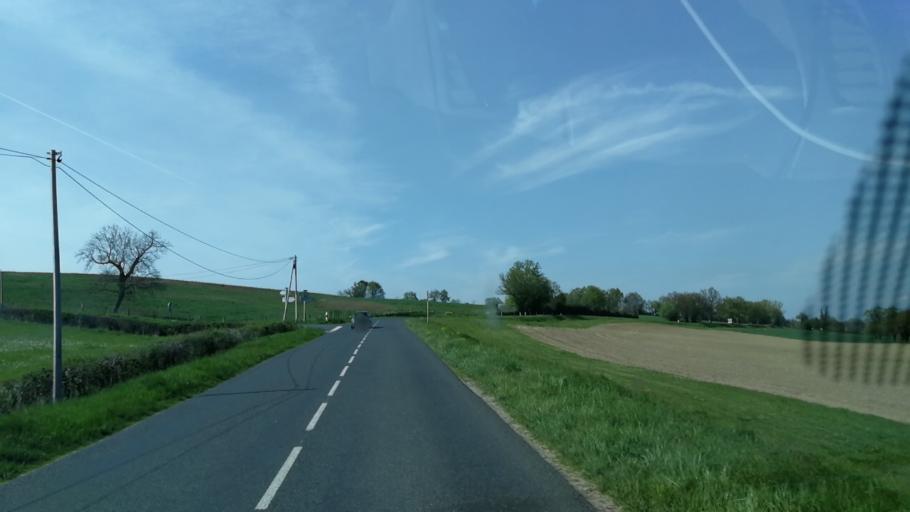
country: FR
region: Auvergne
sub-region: Departement de l'Allier
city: Saint-Gerand-le-Puy
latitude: 46.3568
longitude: 3.5774
